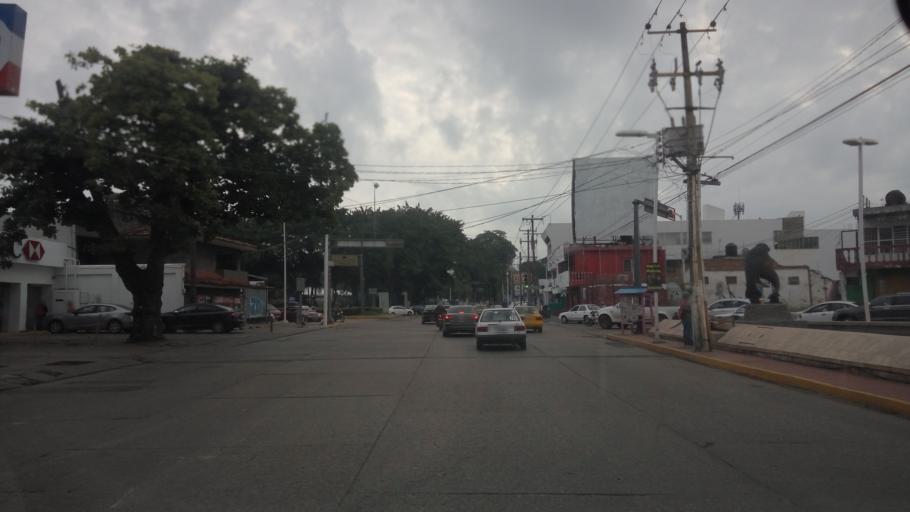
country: MX
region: Tabasco
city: Villahermosa
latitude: 17.9843
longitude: -92.9463
